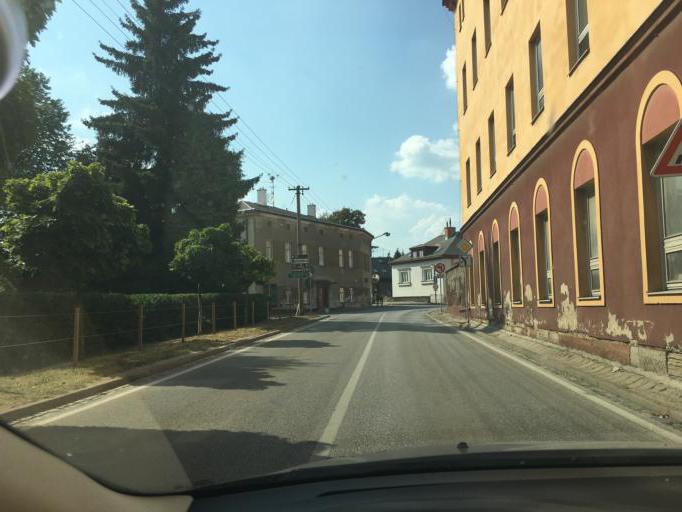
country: CZ
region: Kralovehradecky
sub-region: Okres Trutnov
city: Vrchlabi
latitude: 50.6224
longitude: 15.6158
